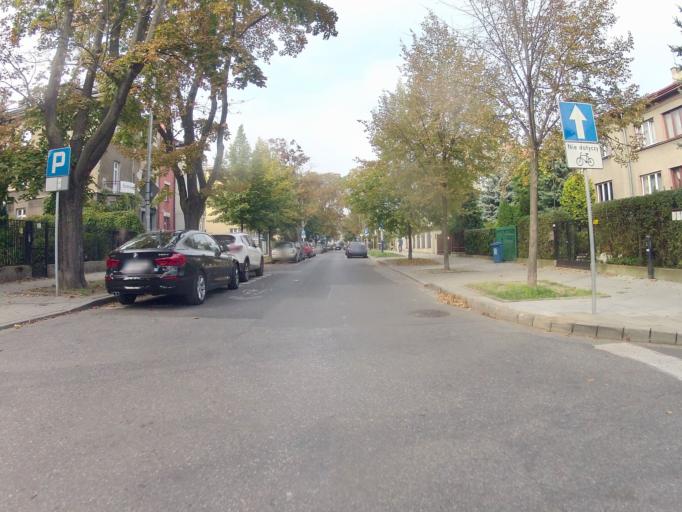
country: PL
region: Lesser Poland Voivodeship
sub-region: Krakow
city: Krakow
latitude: 50.0686
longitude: 19.9629
